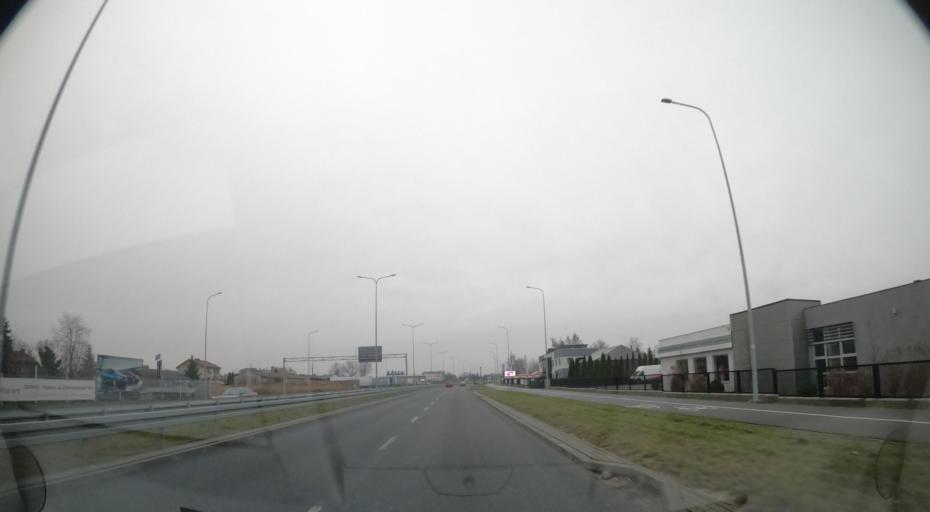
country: PL
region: Masovian Voivodeship
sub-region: Radom
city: Radom
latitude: 51.3915
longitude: 21.1944
